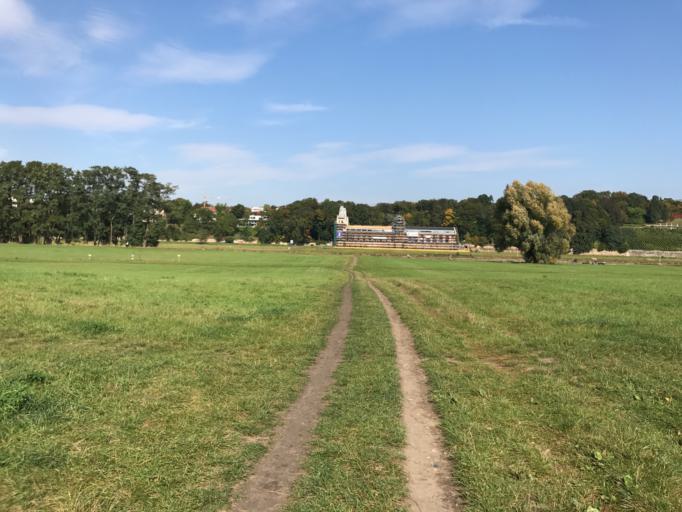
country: DE
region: Saxony
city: Albertstadt
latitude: 51.0611
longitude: 13.7868
